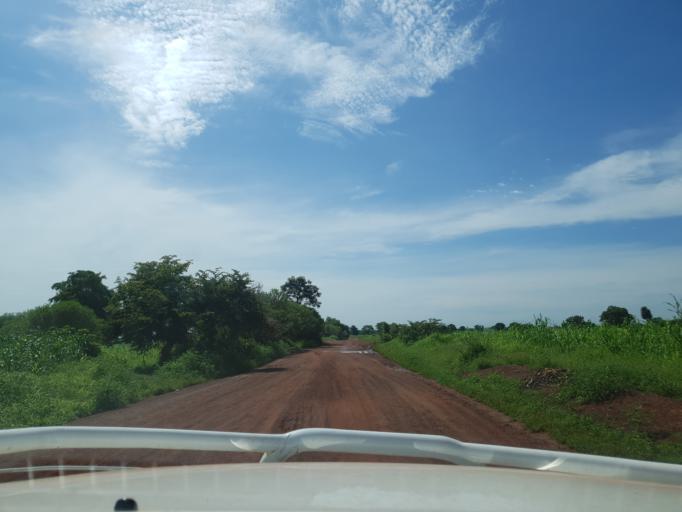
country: ML
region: Koulikoro
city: Banamba
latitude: 13.2786
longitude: -7.5494
